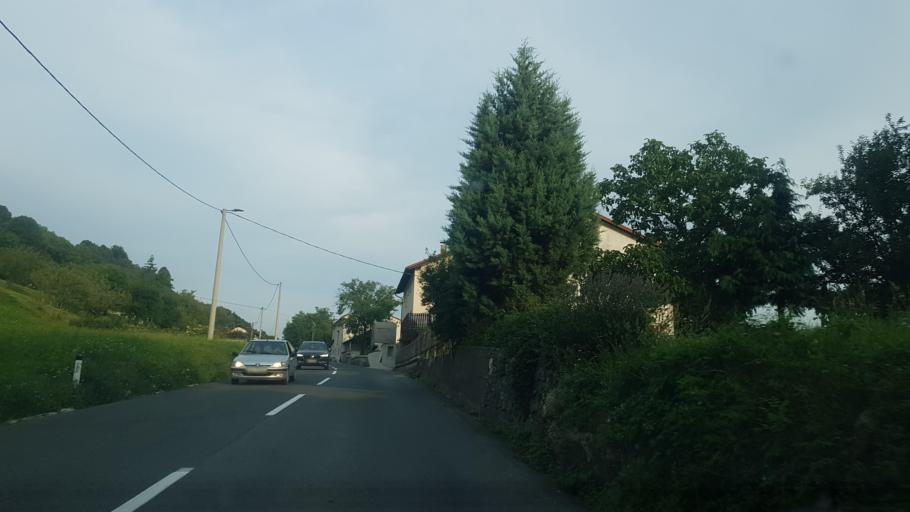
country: SI
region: Vipava
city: Vipava
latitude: 45.8727
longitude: 14.0206
